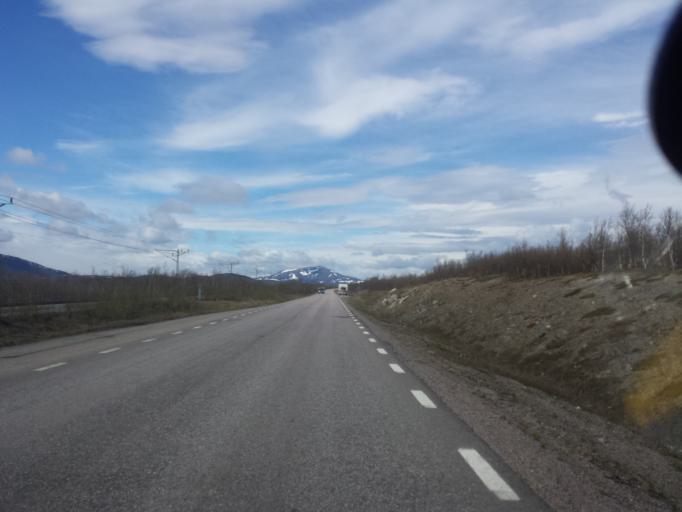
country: SE
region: Norrbotten
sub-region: Kiruna Kommun
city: Kiruna
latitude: 68.0551
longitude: 19.8284
